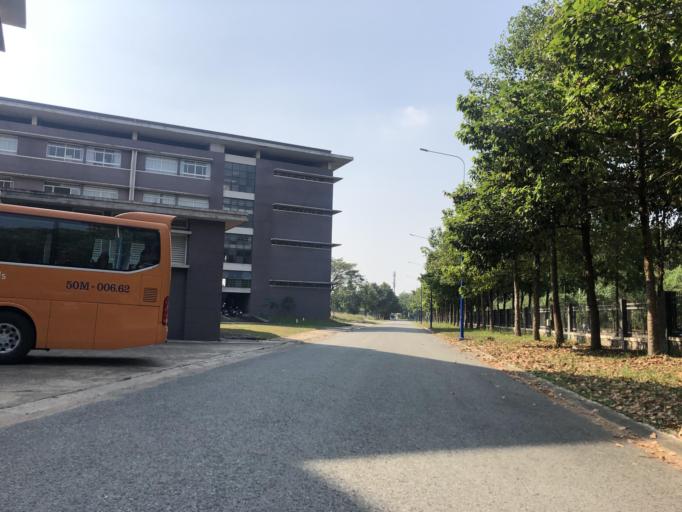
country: VN
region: Binh Duong
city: Thu Dau Mot
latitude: 11.0543
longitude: 106.6645
